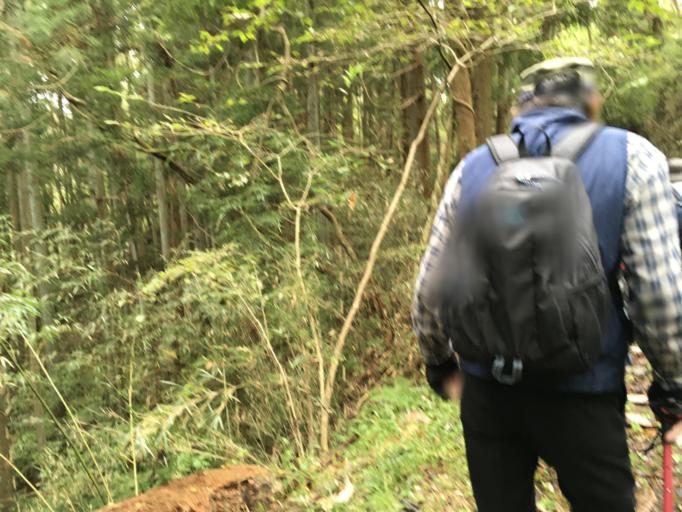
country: JP
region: Iwate
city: Ichinoseki
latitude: 38.8739
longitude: 141.1264
